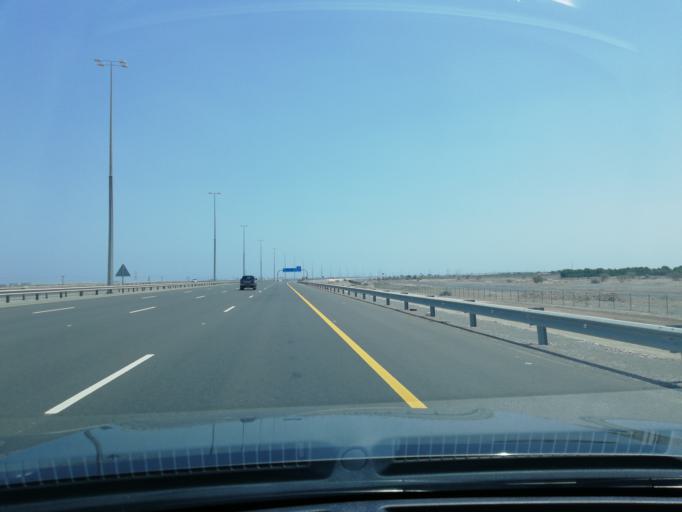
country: OM
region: Al Batinah
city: Barka'
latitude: 23.6252
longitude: 57.8465
